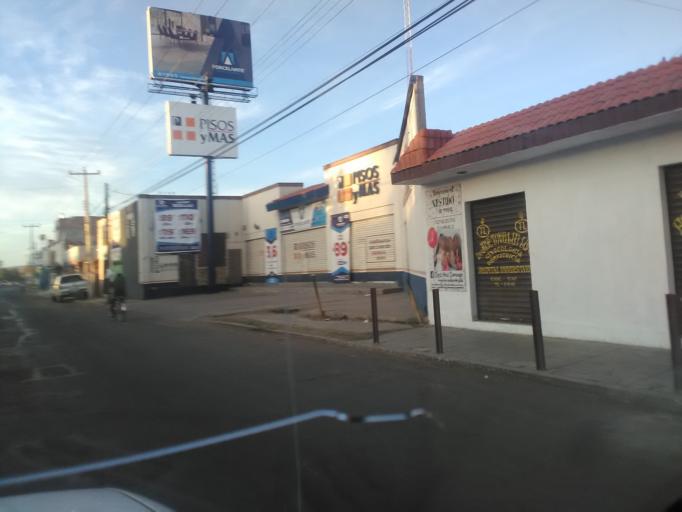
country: MX
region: Durango
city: Victoria de Durango
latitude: 24.0010
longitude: -104.6625
